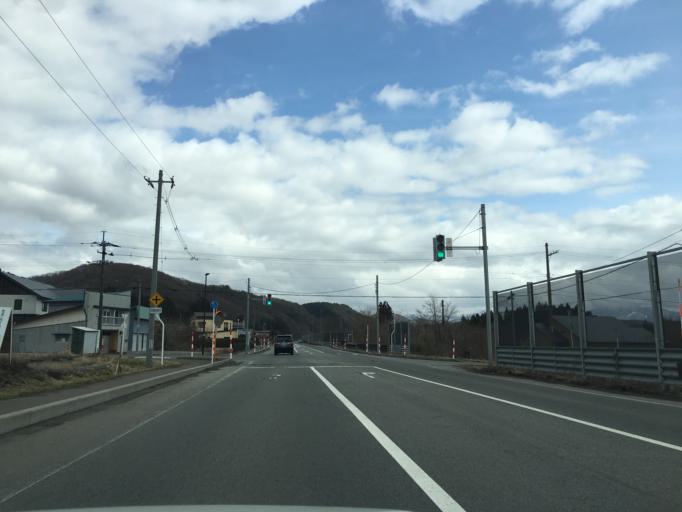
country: JP
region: Akita
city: Hanawa
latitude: 40.2333
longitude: 140.6939
